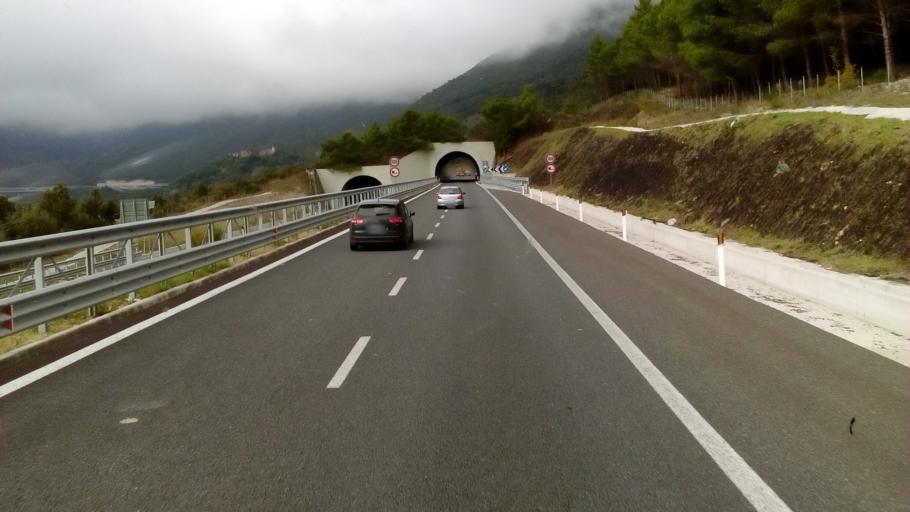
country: IT
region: Calabria
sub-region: Provincia di Cosenza
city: Morano Calabro
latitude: 39.8812
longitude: 16.1624
